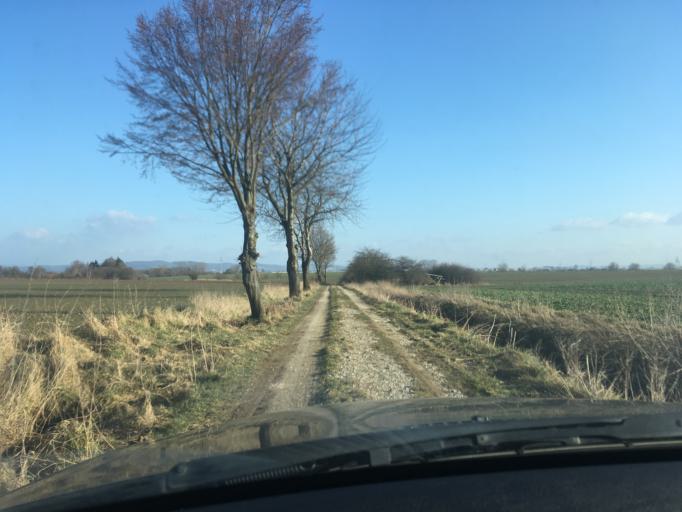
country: DE
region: Lower Saxony
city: Einbeck
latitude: 51.8039
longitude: 9.8171
